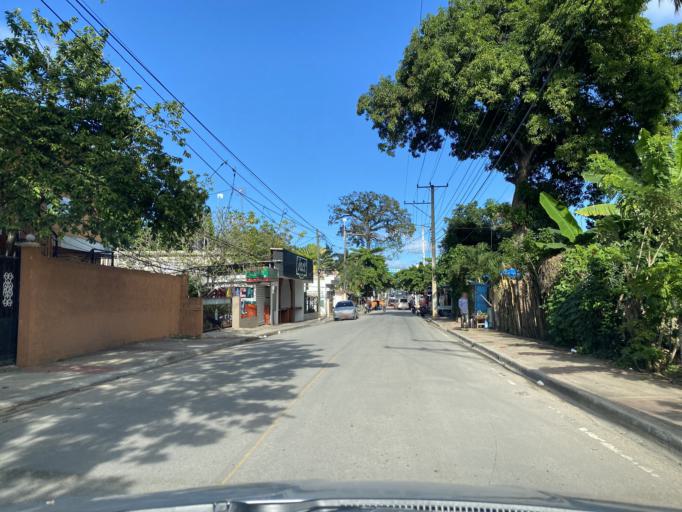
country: DO
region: Samana
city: Las Terrenas
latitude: 19.3039
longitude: -69.5502
